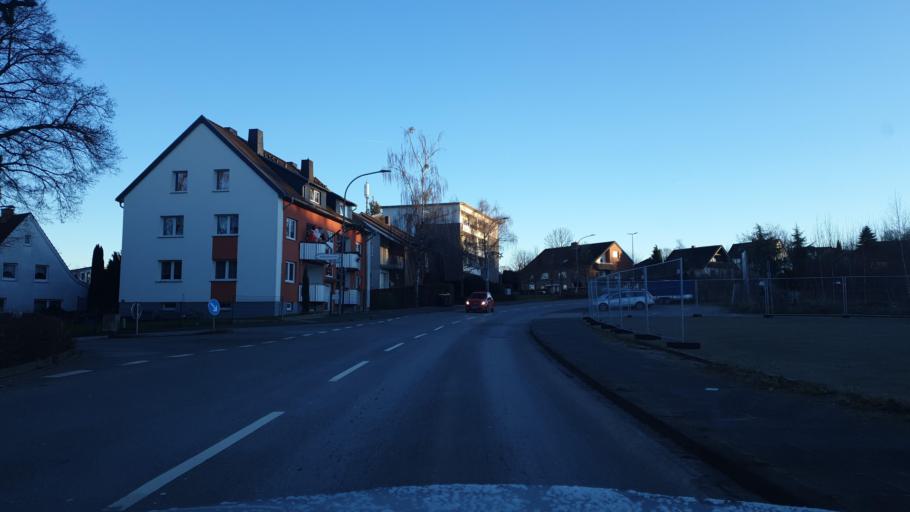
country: DE
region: North Rhine-Westphalia
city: Bad Oeynhausen
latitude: 52.1918
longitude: 8.8026
